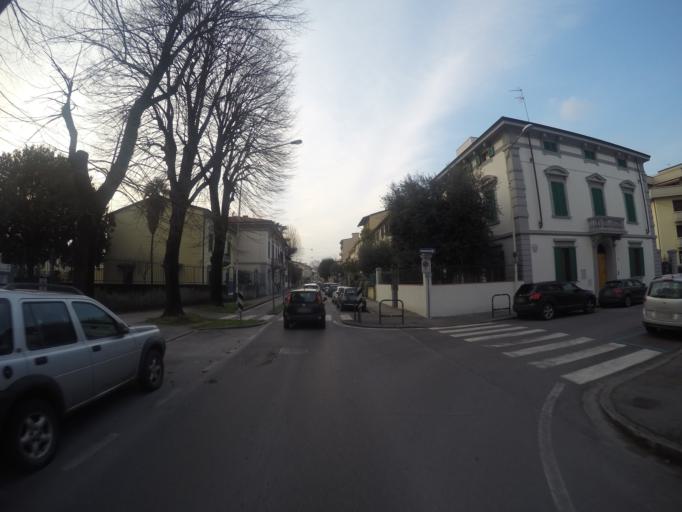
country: IT
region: Tuscany
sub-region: Provincia di Prato
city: Prato
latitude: 43.8800
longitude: 11.1050
